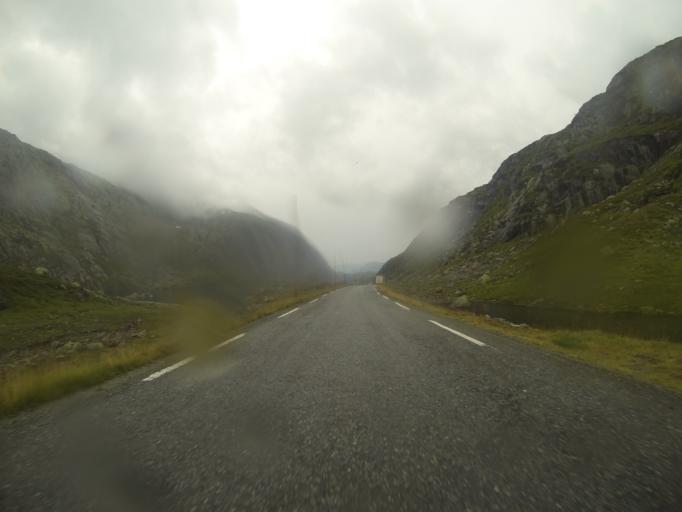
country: NO
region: Hordaland
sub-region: Odda
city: Odda
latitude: 59.7604
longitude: 6.7181
